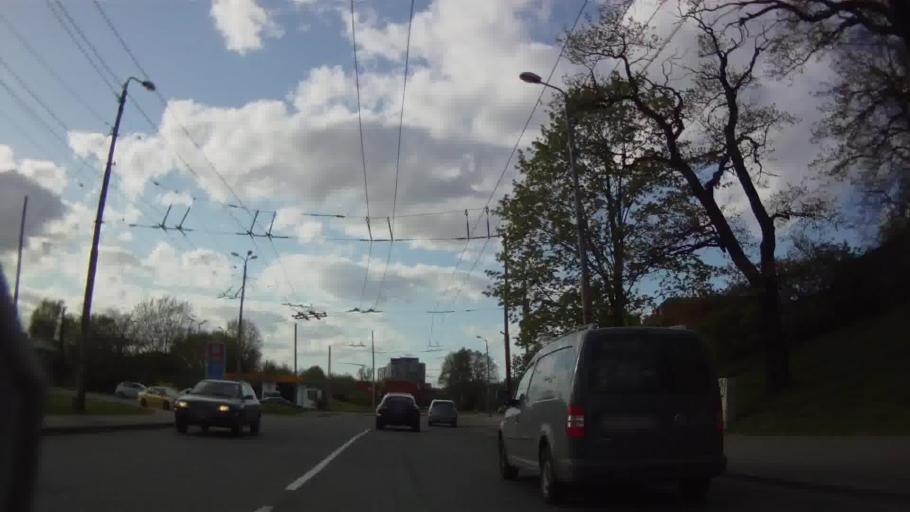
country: LV
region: Riga
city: Riga
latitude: 56.9881
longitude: 24.1311
